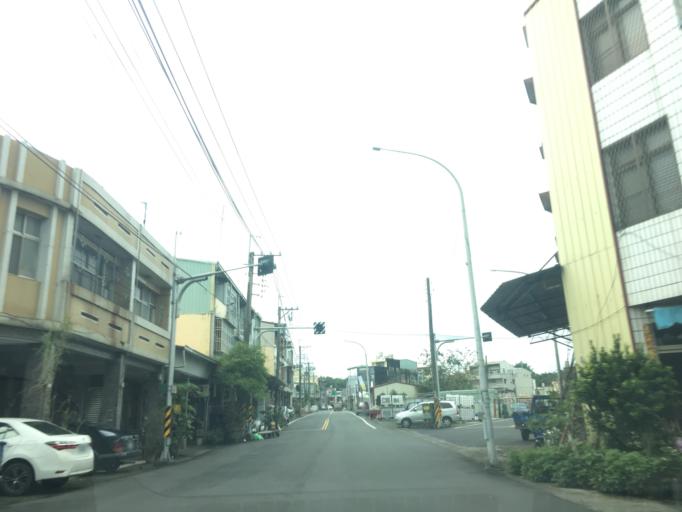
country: TW
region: Taiwan
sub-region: Yunlin
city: Douliu
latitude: 23.5878
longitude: 120.5552
